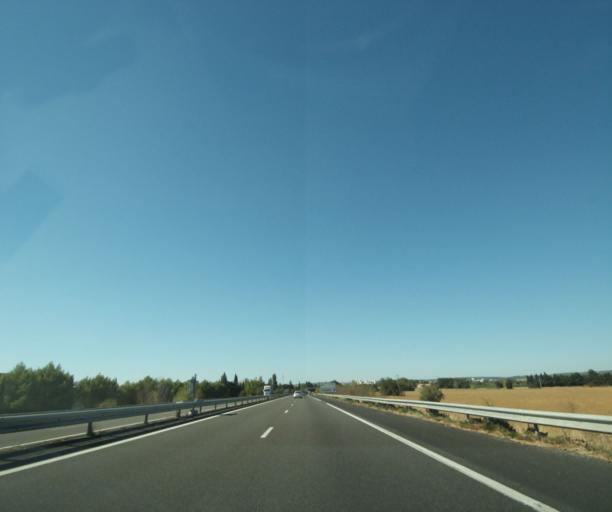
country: FR
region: Languedoc-Roussillon
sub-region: Departement du Gard
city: Caissargues
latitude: 43.7964
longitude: 4.3900
